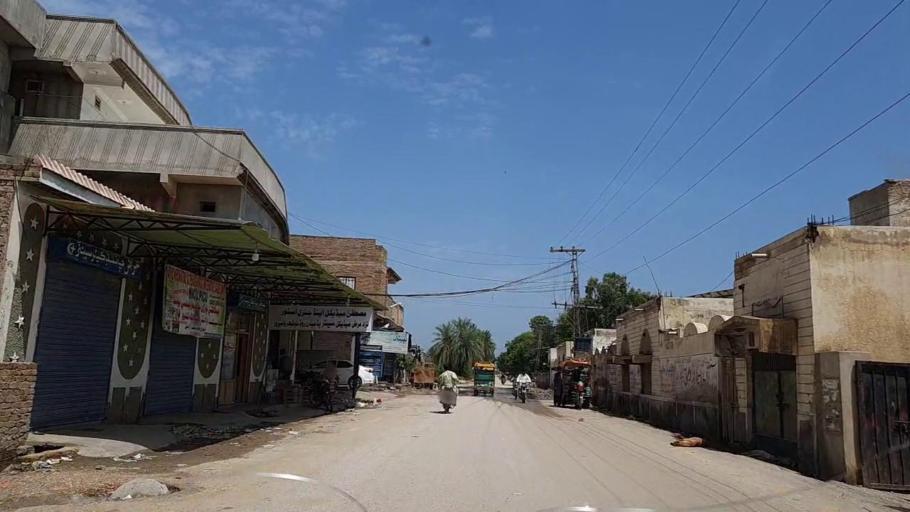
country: PK
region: Sindh
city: Naushahro Firoz
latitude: 26.8360
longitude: 68.1243
